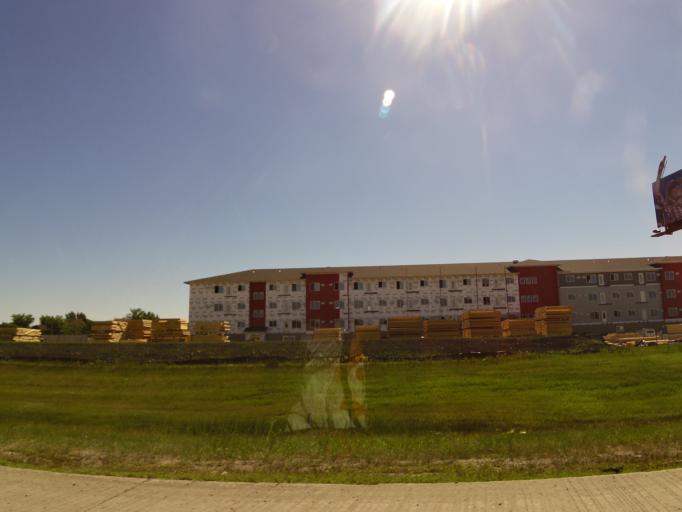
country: US
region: North Dakota
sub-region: Cass County
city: Fargo
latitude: 46.8523
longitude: -96.8406
